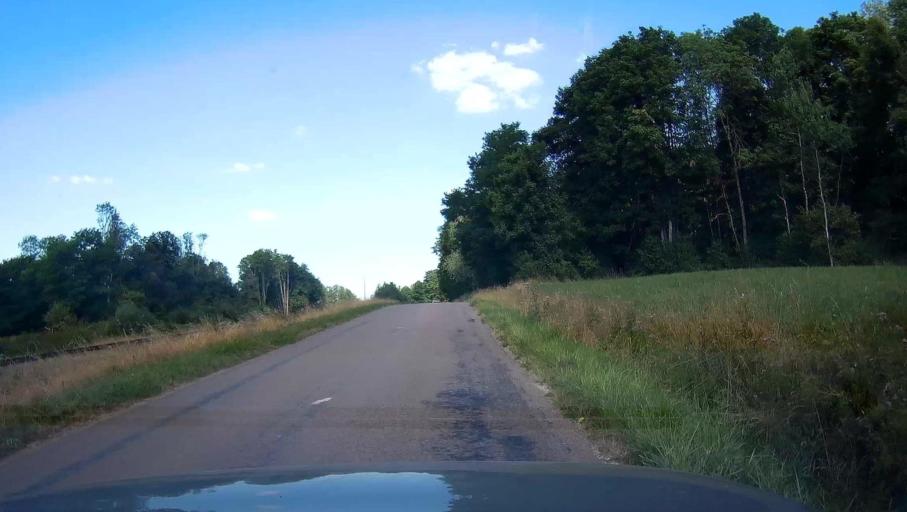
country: FR
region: Champagne-Ardenne
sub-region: Departement de la Haute-Marne
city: Langres
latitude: 47.8586
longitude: 5.3713
